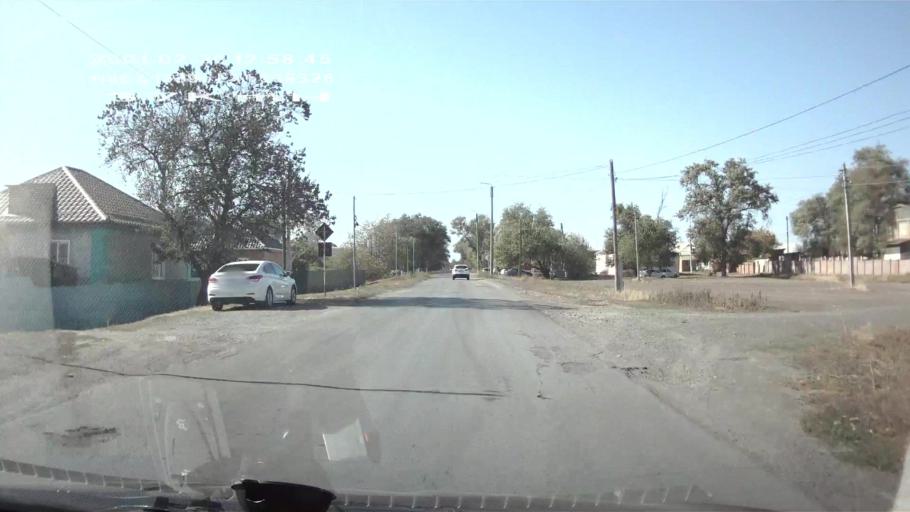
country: RU
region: Rostov
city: Gigant
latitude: 46.5131
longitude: 41.3386
